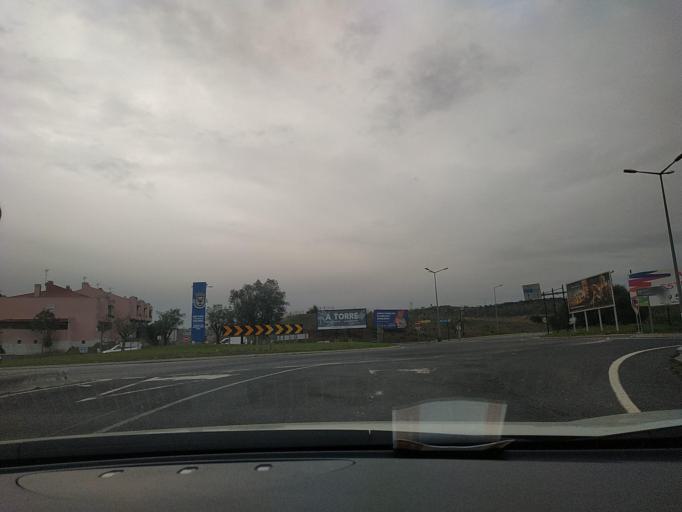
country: PT
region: Lisbon
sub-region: Loures
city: Santa Iria da Azoia
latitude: 38.8631
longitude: -9.1037
